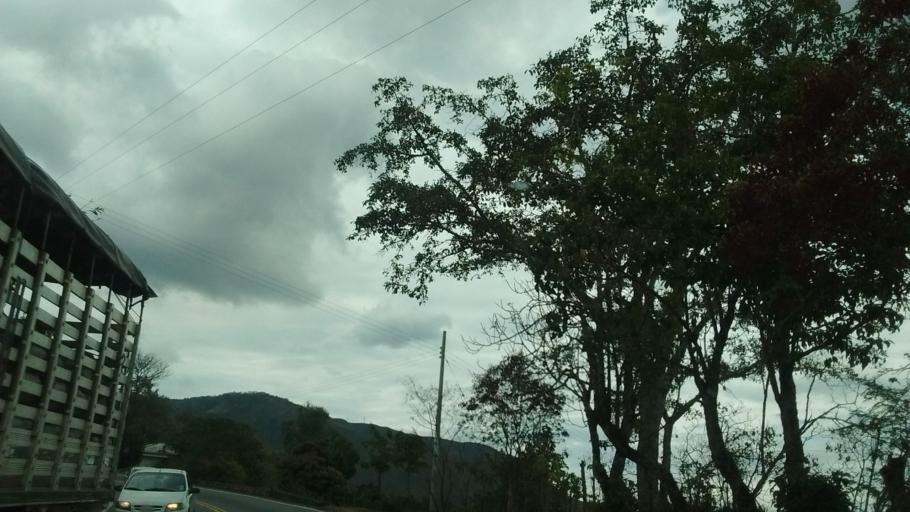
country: CO
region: Cauca
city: Rosas
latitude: 2.2747
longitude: -76.7226
